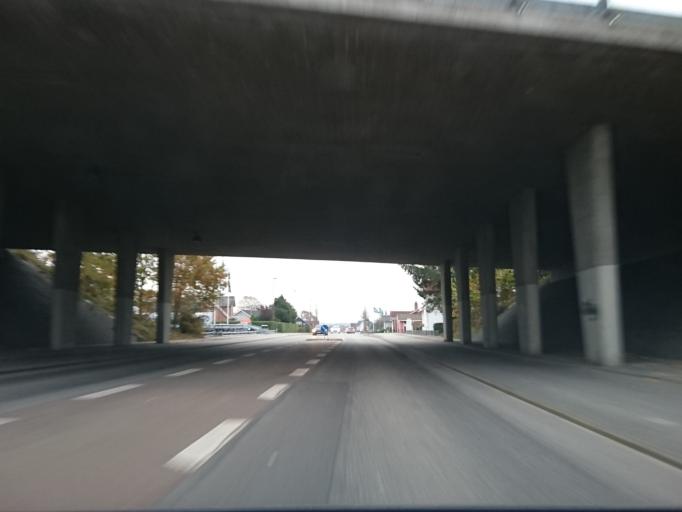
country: DK
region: North Denmark
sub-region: Alborg Kommune
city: Aalborg
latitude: 57.0121
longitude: 9.9256
